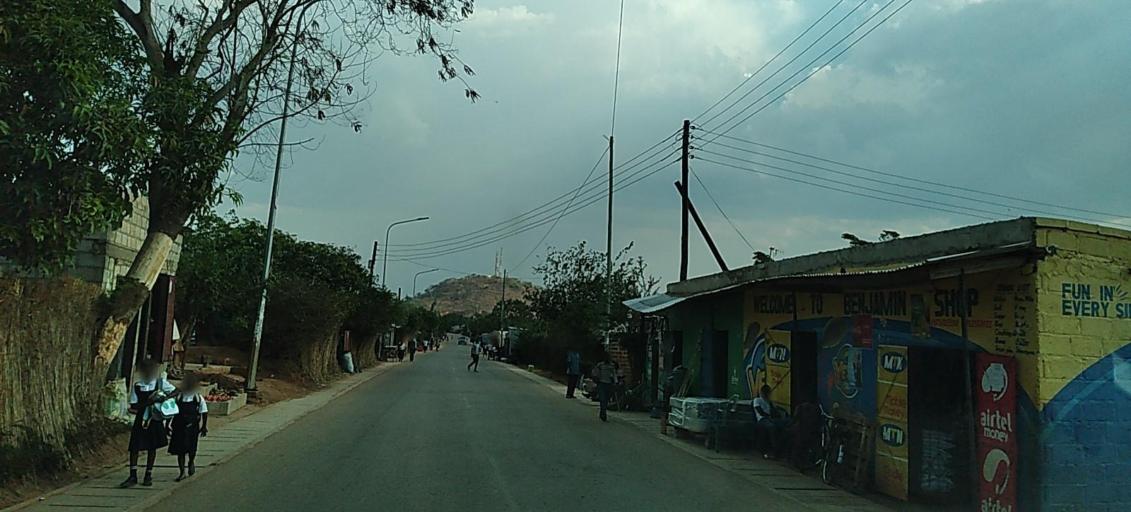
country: ZM
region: Lusaka
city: Lusaka
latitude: -15.5331
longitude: 28.2370
